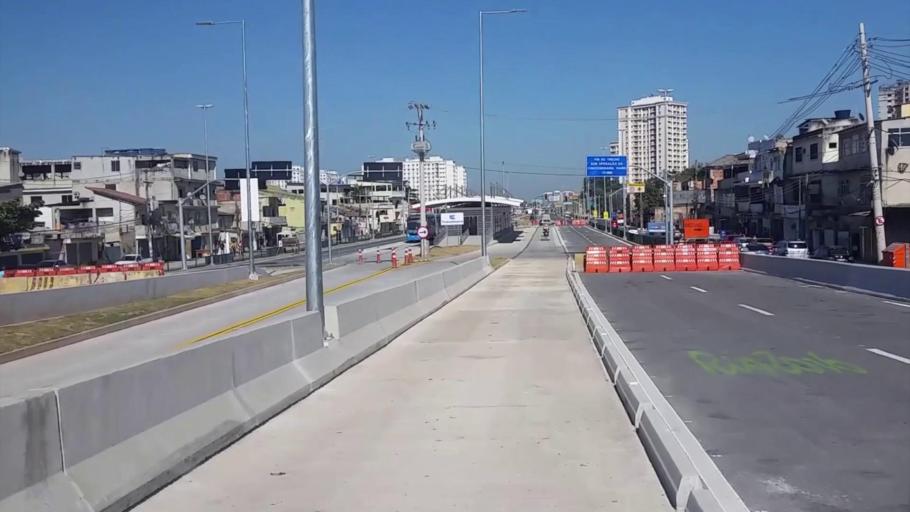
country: BR
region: Rio de Janeiro
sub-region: Nilopolis
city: Nilopolis
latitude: -22.9540
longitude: -43.3914
